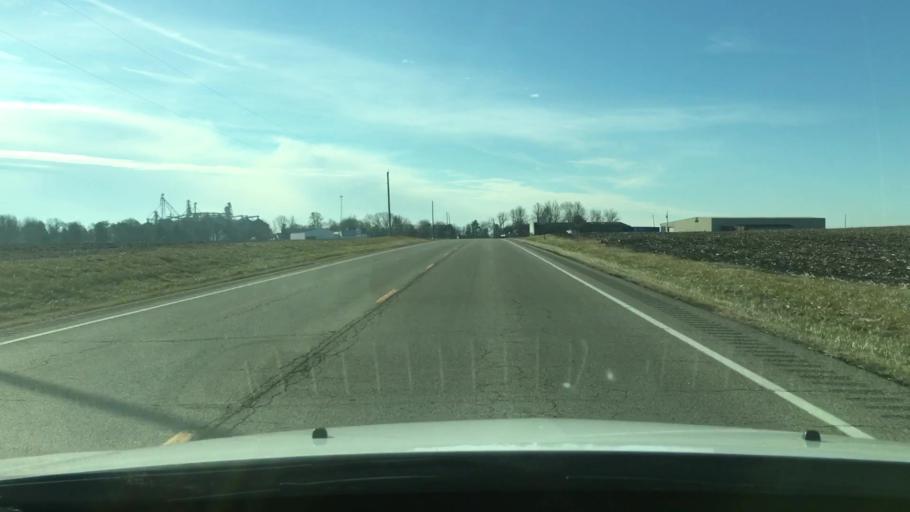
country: US
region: Illinois
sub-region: Marshall County
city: Toluca
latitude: 41.0457
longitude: -89.2261
